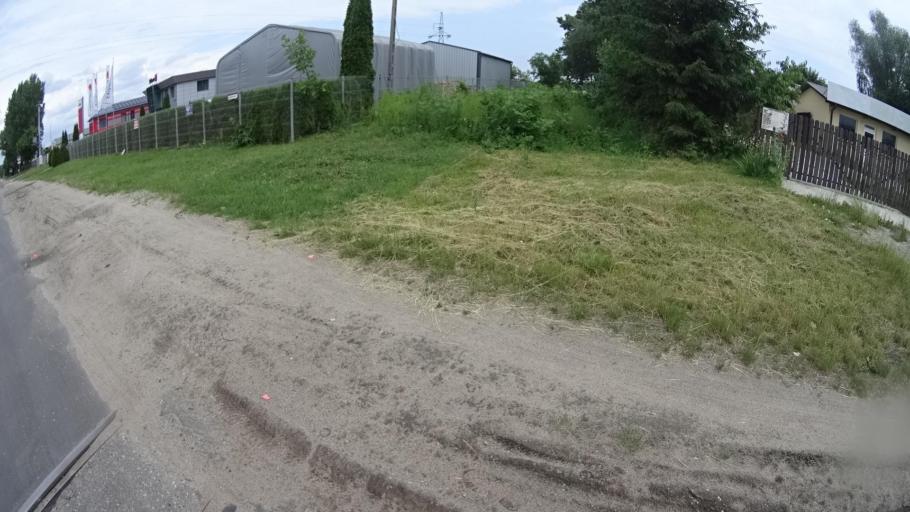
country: PL
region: Masovian Voivodeship
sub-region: Powiat grojecki
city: Grojec
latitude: 51.8494
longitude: 20.8722
